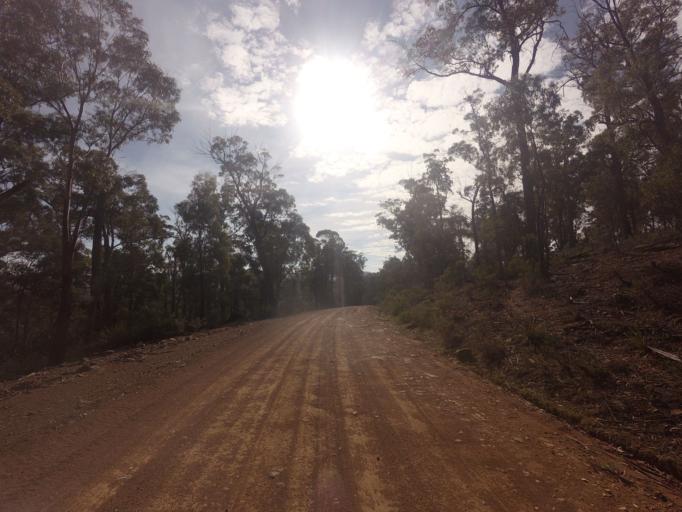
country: AU
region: Tasmania
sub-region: Sorell
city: Sorell
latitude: -42.5385
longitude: 147.4535
